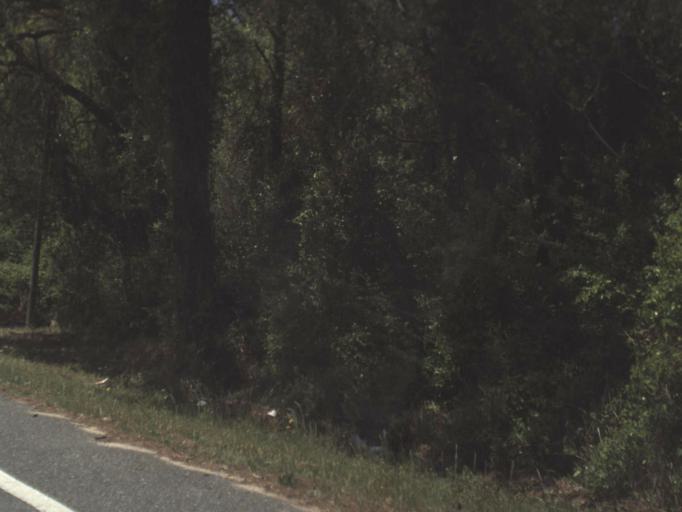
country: US
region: Florida
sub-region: Escambia County
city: Bellview
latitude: 30.4976
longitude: -87.3331
